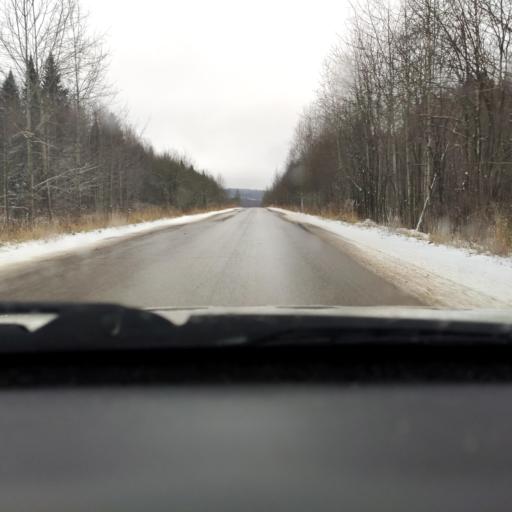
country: RU
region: Perm
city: Ferma
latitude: 57.9873
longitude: 56.3695
